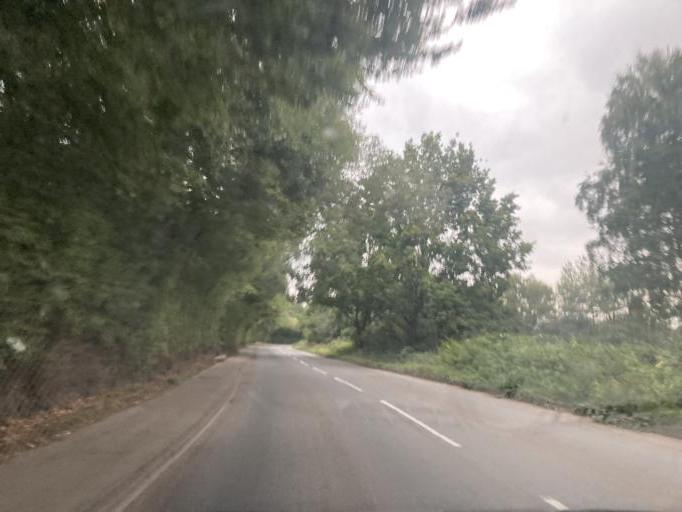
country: GB
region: England
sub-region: Surrey
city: Bagshot
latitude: 51.3624
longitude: -0.6787
